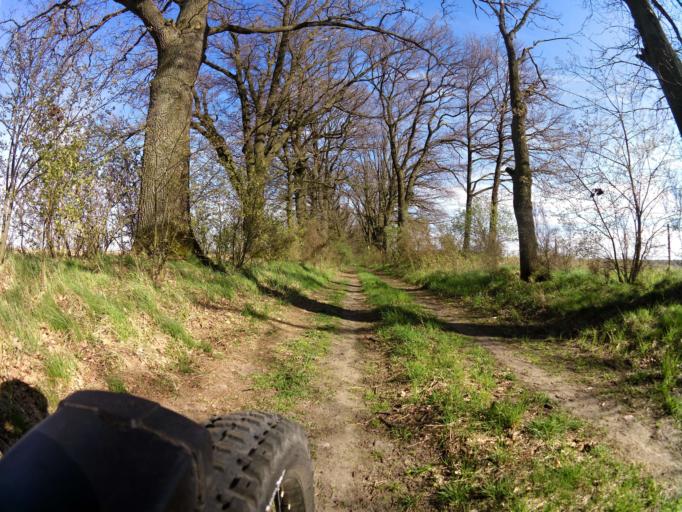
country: PL
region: West Pomeranian Voivodeship
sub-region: Powiat lobeski
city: Resko
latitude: 53.7842
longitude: 15.5467
